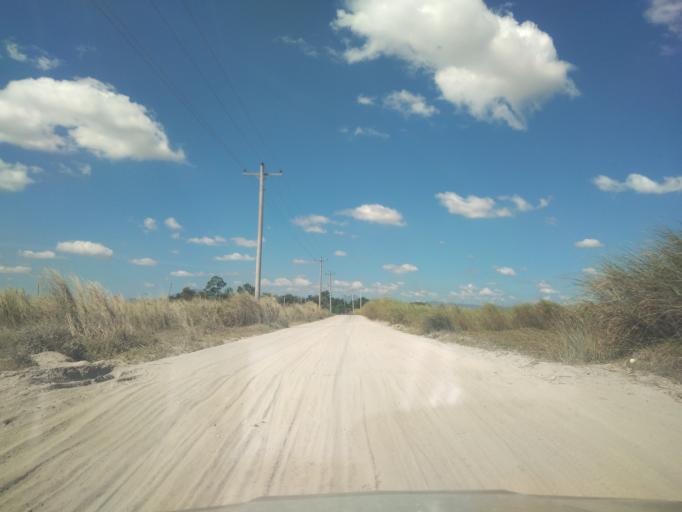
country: PH
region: Central Luzon
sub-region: Province of Pampanga
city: Balas
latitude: 15.0605
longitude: 120.5937
